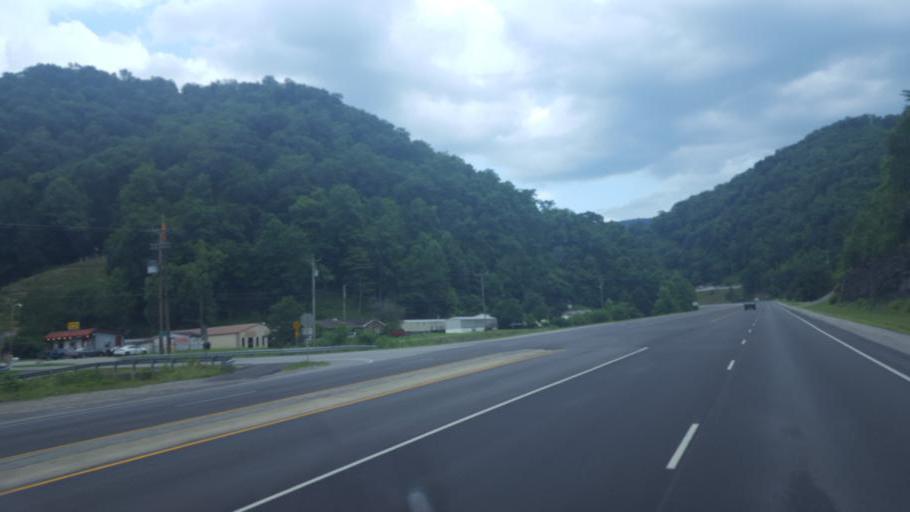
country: US
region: Kentucky
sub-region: Letcher County
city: Jenkins
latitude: 37.3151
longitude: -82.5495
